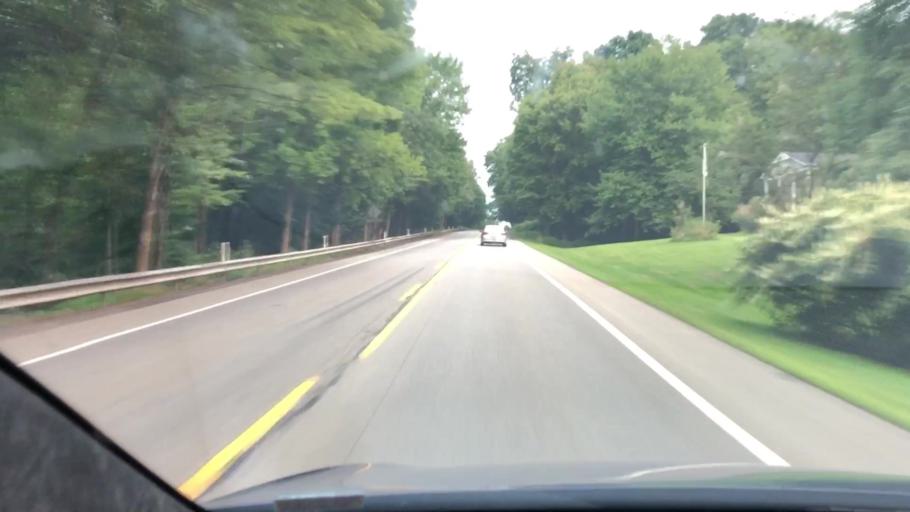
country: US
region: Pennsylvania
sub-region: Butler County
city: Slippery Rock
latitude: 41.0022
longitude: -79.9947
